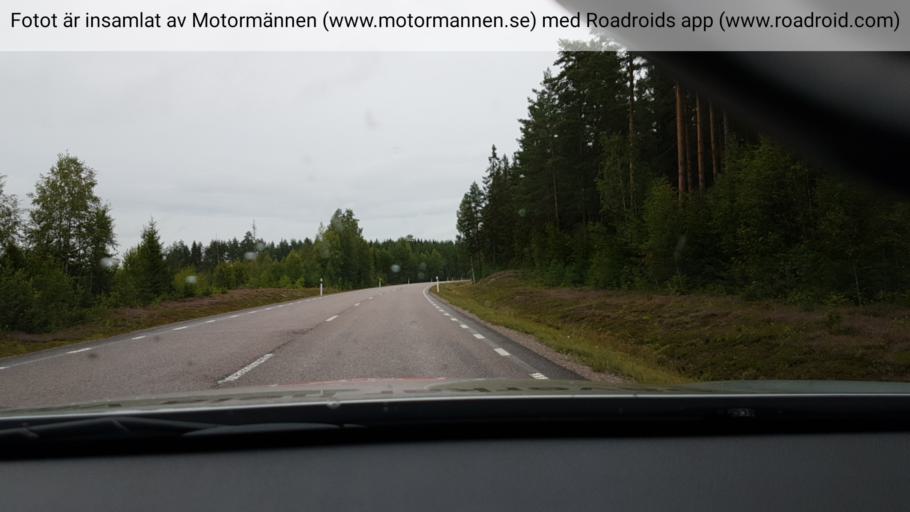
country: SE
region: Gaevleborg
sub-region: Gavle Kommun
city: Hedesunda
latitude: 60.4066
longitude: 16.9725
